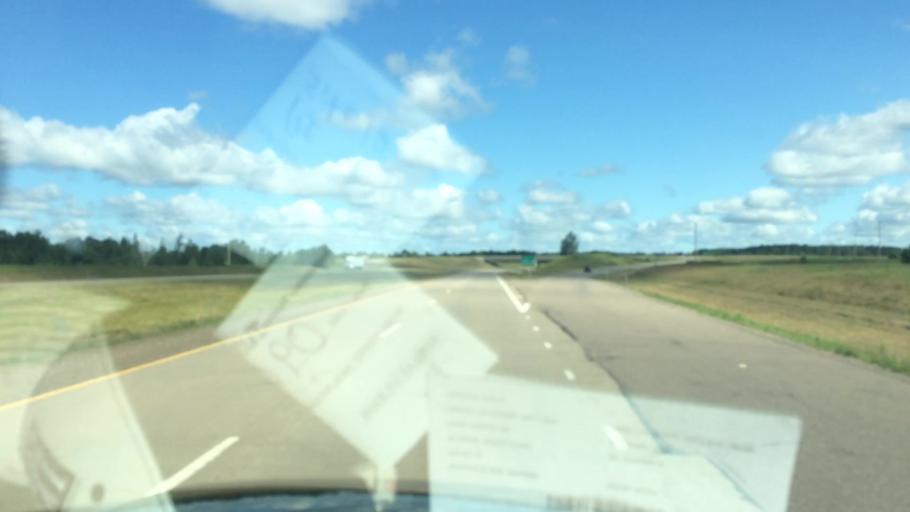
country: US
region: Wisconsin
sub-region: Lincoln County
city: Tomahawk
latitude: 45.4912
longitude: -89.6955
